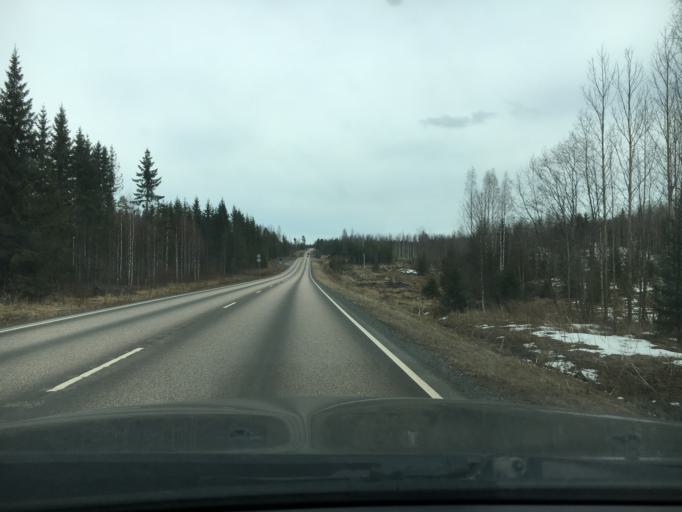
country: FI
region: Central Finland
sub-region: AEaenekoski
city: Konnevesi
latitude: 62.6917
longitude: 26.4147
